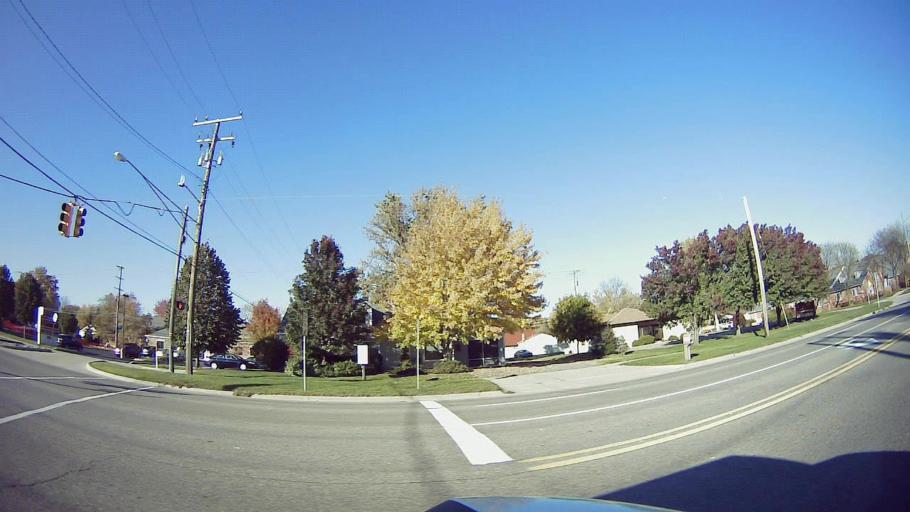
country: US
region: Michigan
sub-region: Oakland County
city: Clawson
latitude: 42.5484
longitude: -83.1404
